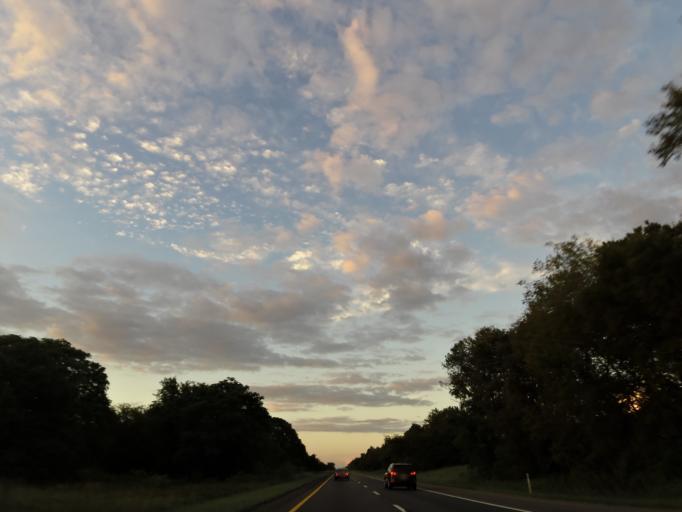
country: US
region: Tennessee
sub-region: Monroe County
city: Sweetwater
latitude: 35.6493
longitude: -84.4643
